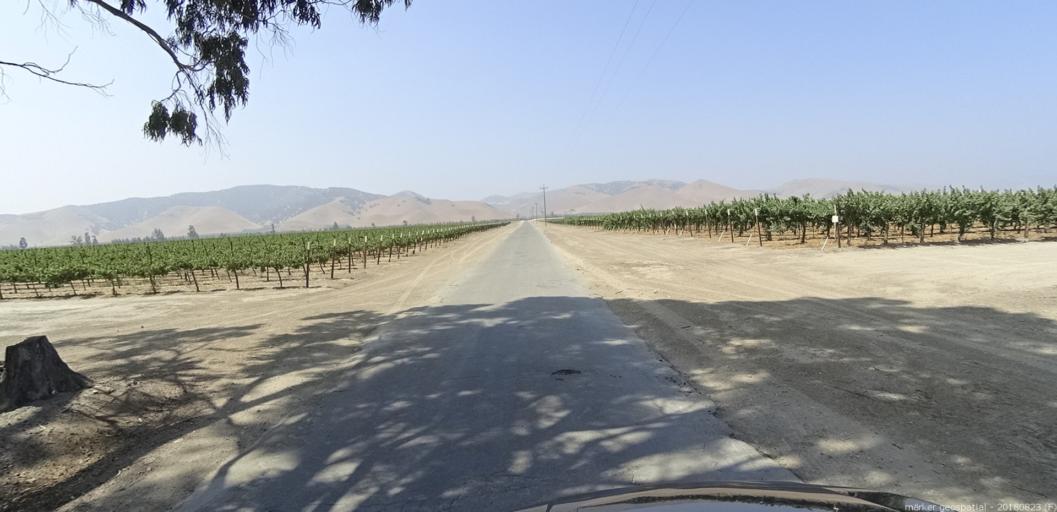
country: US
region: California
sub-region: Monterey County
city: Greenfield
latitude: 36.2663
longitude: -121.2029
